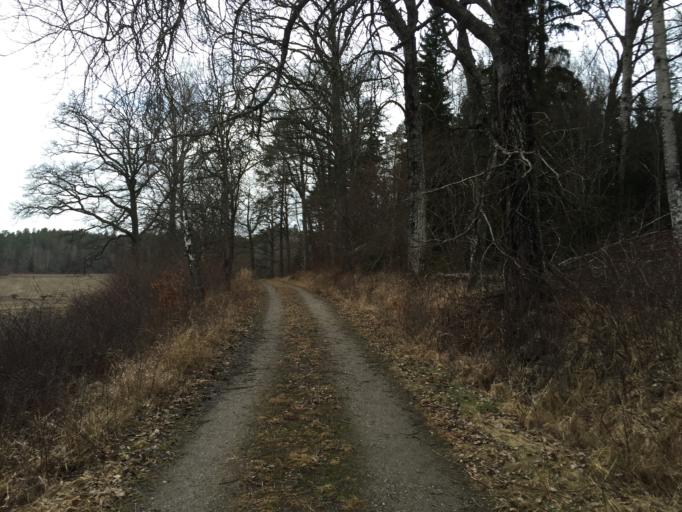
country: SE
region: Stockholm
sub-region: Salems Kommun
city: Ronninge
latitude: 59.2505
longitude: 17.7031
